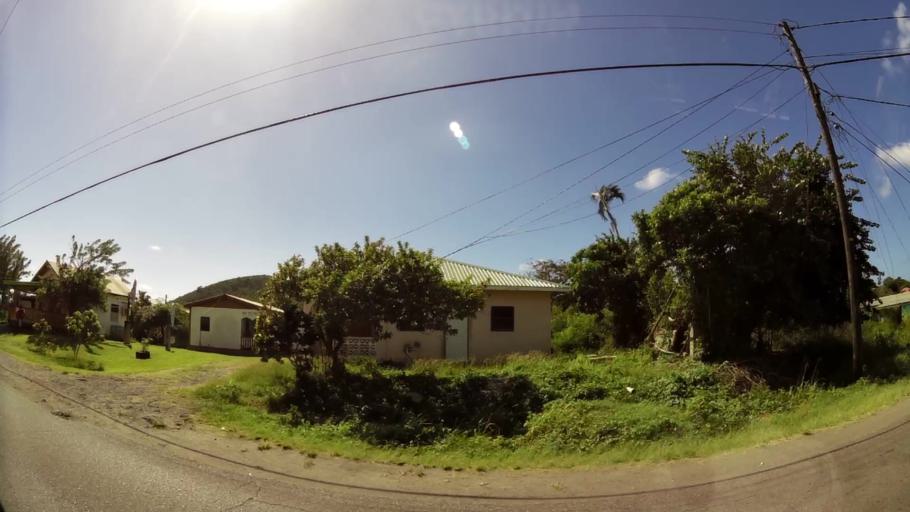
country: LC
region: Laborie Quarter
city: Laborie
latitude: 13.7503
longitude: -60.9659
